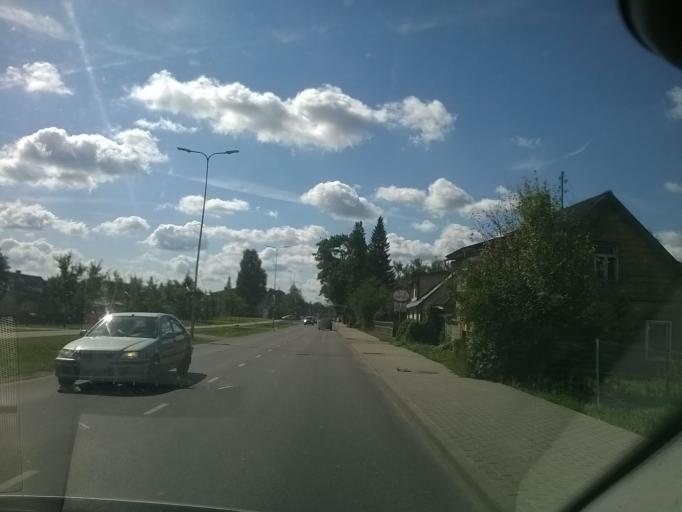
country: EE
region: Vorumaa
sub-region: Voru linn
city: Voru
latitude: 57.8404
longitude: 27.0069
